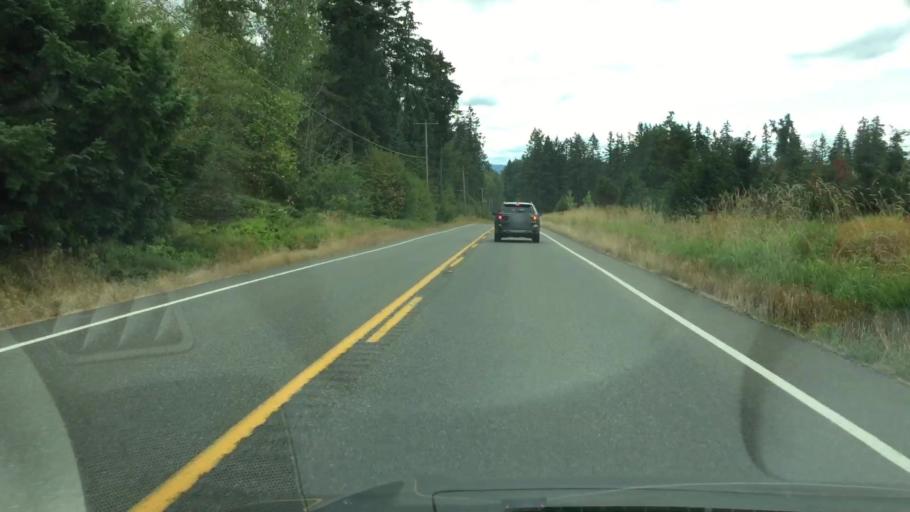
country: US
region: Washington
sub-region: Pierce County
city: Graham
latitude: 46.9582
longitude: -122.2974
